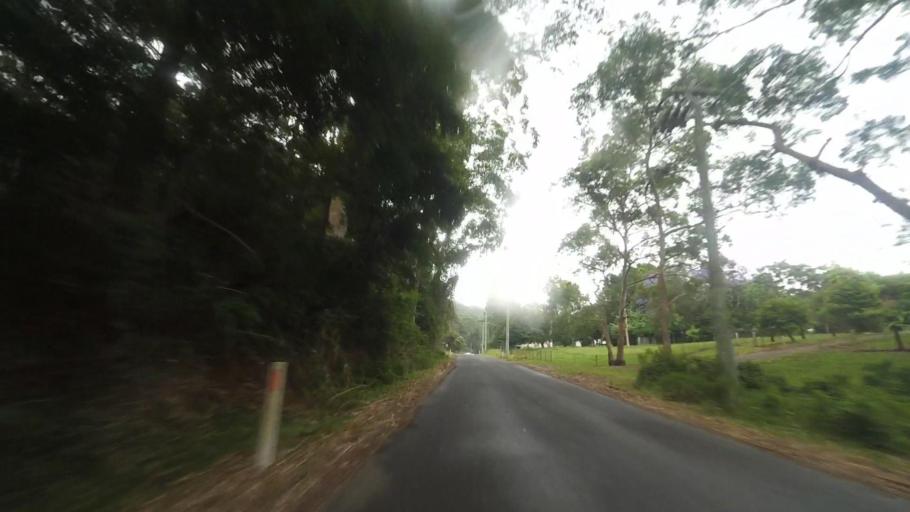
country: AU
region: New South Wales
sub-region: Wollongong
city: Cordeaux Heights
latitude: -34.4322
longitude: 150.8061
